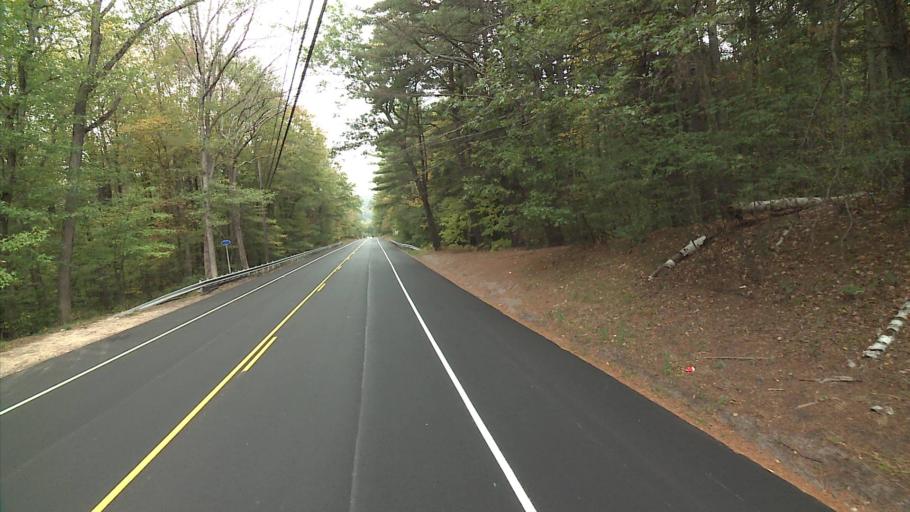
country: US
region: Connecticut
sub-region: Litchfield County
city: Thomaston
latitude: 41.6459
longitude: -73.0943
